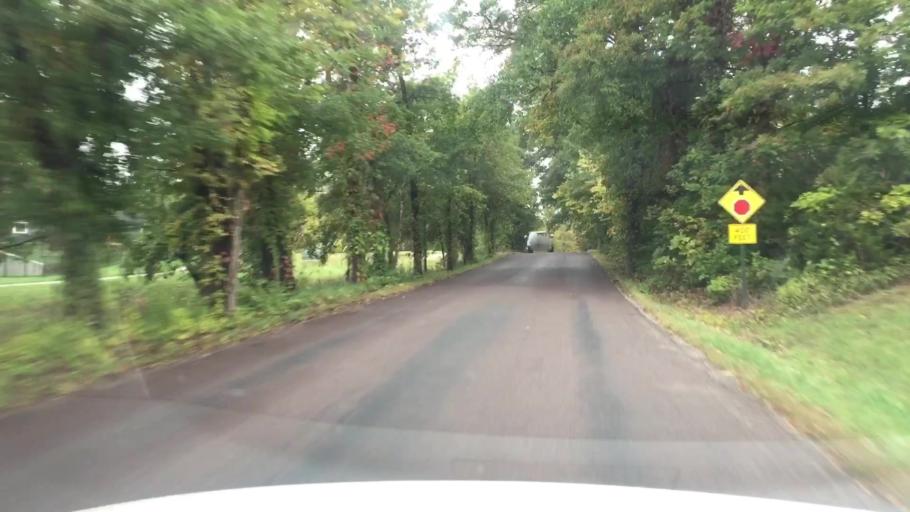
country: US
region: Missouri
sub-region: Boone County
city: Columbia
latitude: 38.8709
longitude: -92.3738
